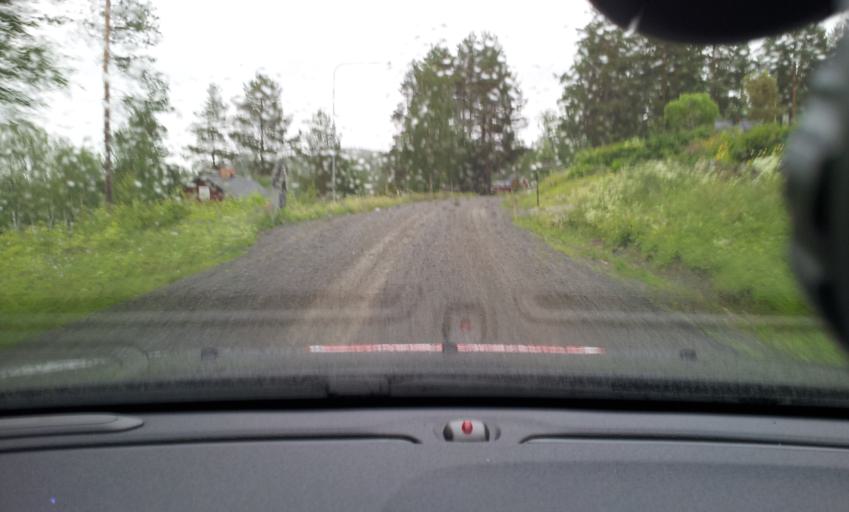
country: SE
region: Jaemtland
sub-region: Ragunda Kommun
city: Hammarstrand
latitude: 63.1329
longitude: 16.1222
